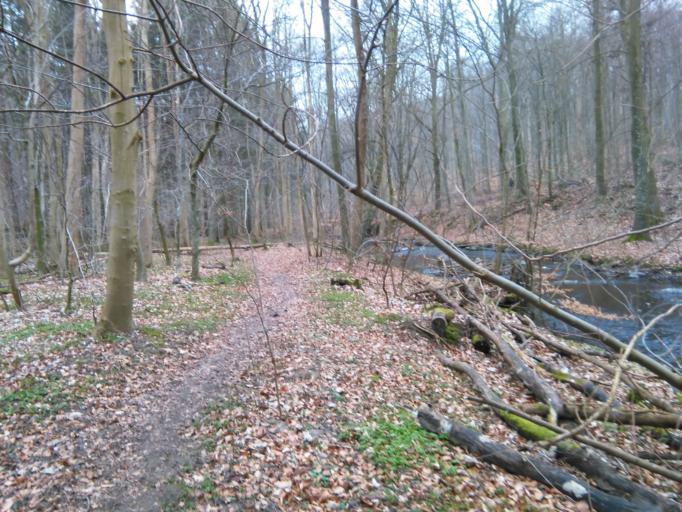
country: DK
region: Central Jutland
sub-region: Arhus Kommune
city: Beder
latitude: 56.0686
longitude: 10.1956
